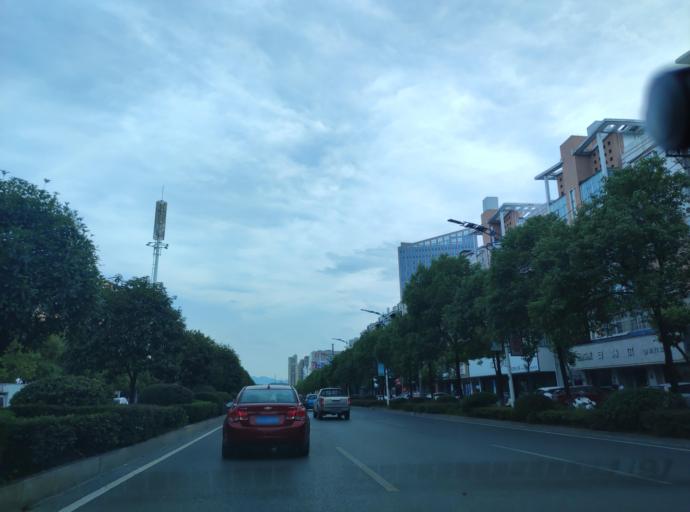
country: CN
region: Jiangxi Sheng
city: Pingxiang
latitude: 27.6399
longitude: 113.8706
